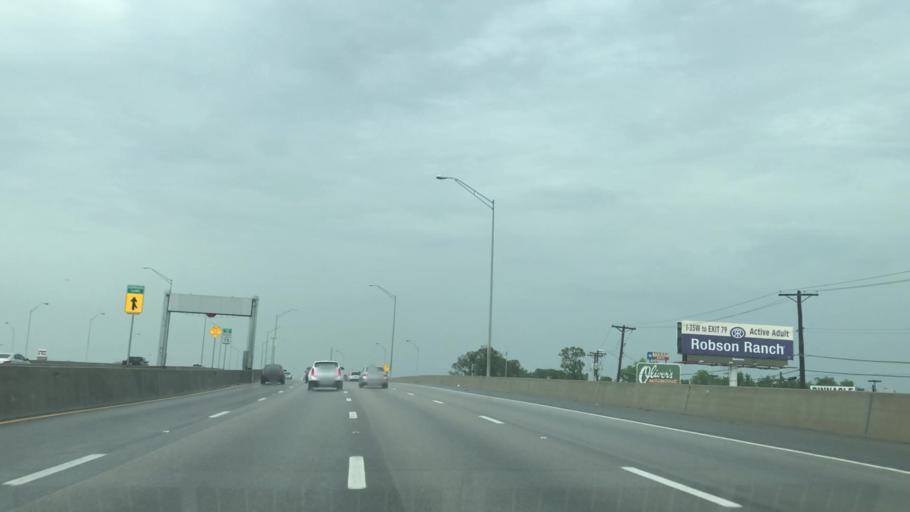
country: US
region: Texas
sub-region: Denton County
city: Lewisville
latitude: 33.0282
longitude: -96.9906
